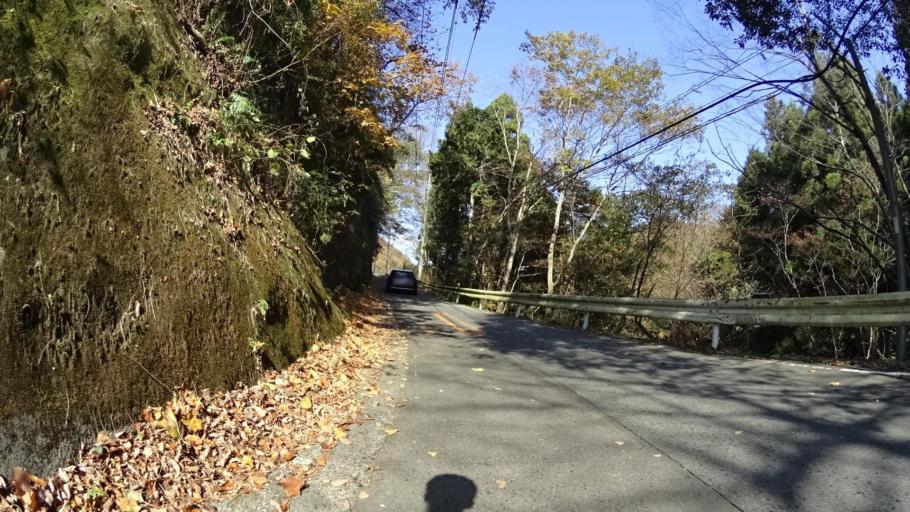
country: JP
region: Yamanashi
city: Uenohara
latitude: 35.5821
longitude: 139.1555
